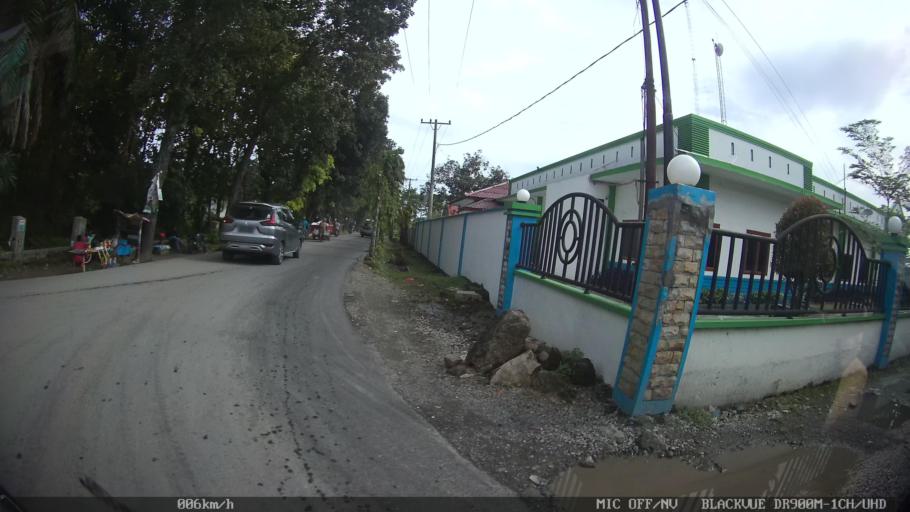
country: ID
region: North Sumatra
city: Medan
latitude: 3.6216
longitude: 98.7142
